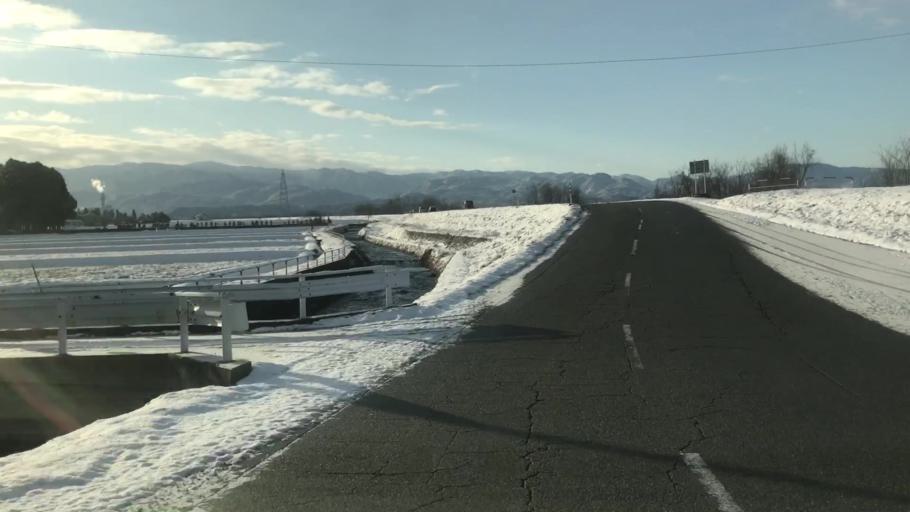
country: JP
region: Toyama
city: Toyama-shi
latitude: 36.6459
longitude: 137.2868
